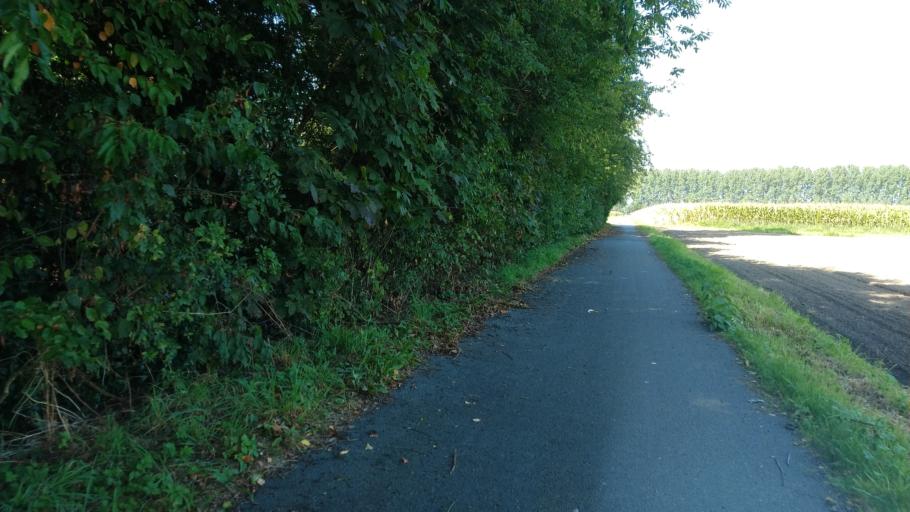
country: NL
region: Zeeland
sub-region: Gemeente Terneuzen
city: Sas van Gent
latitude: 51.2102
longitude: 3.7893
